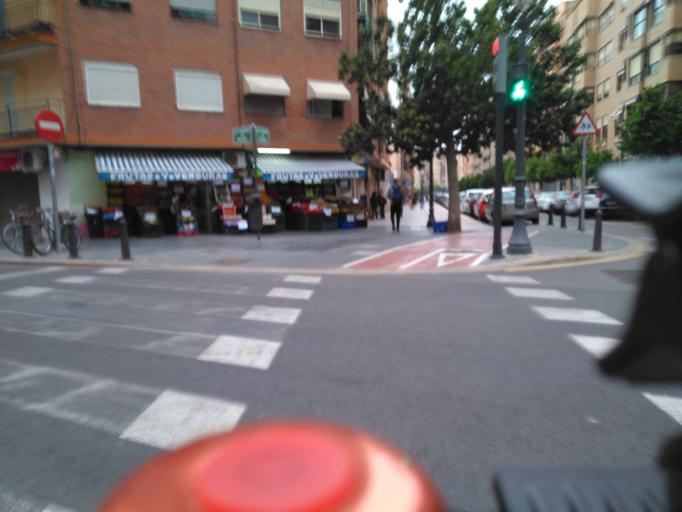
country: ES
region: Valencia
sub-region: Provincia de Valencia
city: Mislata
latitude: 39.4719
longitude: -0.3990
